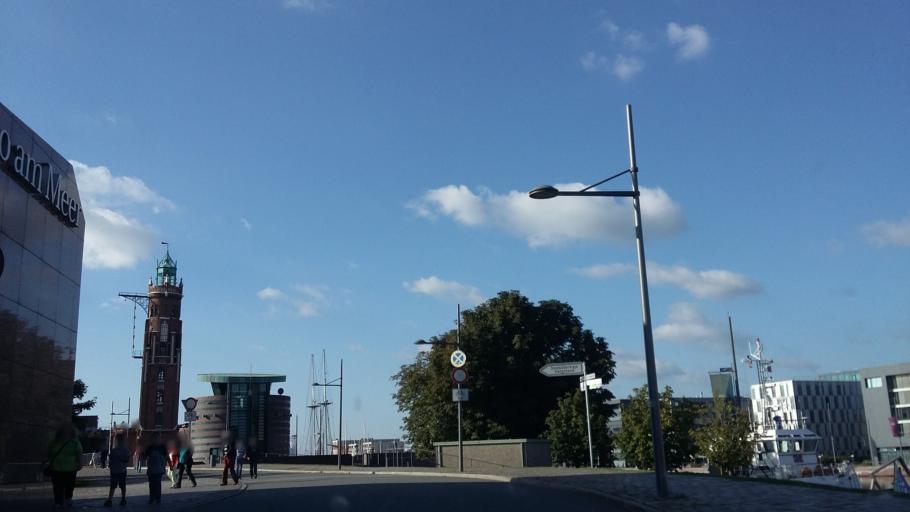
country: DE
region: Bremen
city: Bremerhaven
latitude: 53.5452
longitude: 8.5710
